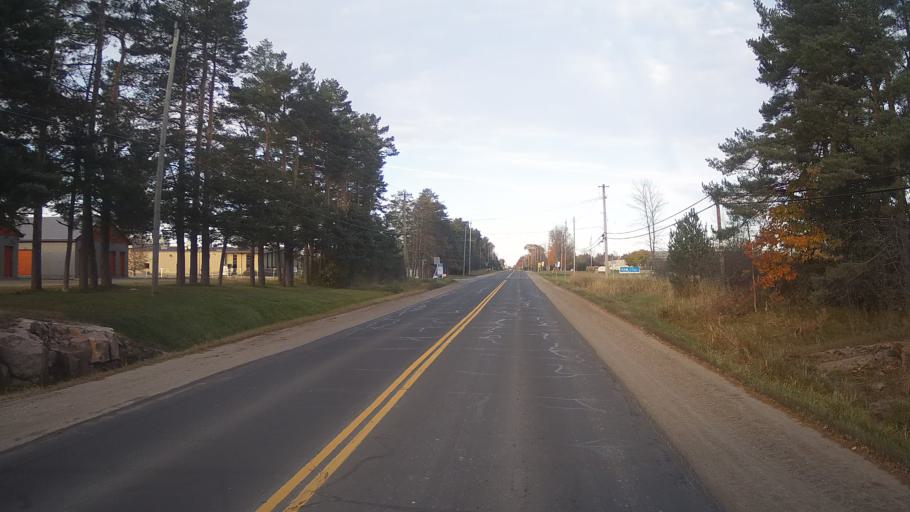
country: CA
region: Ontario
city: Perth
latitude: 44.8866
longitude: -76.2498
